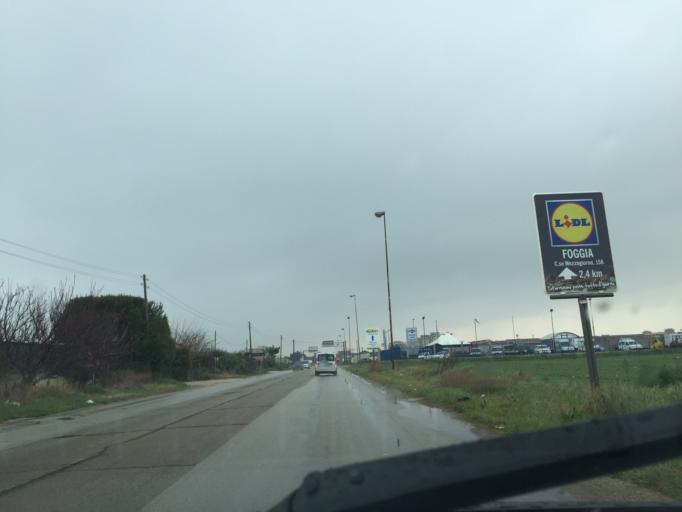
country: IT
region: Apulia
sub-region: Provincia di Foggia
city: Foggia
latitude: 41.4701
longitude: 15.5147
